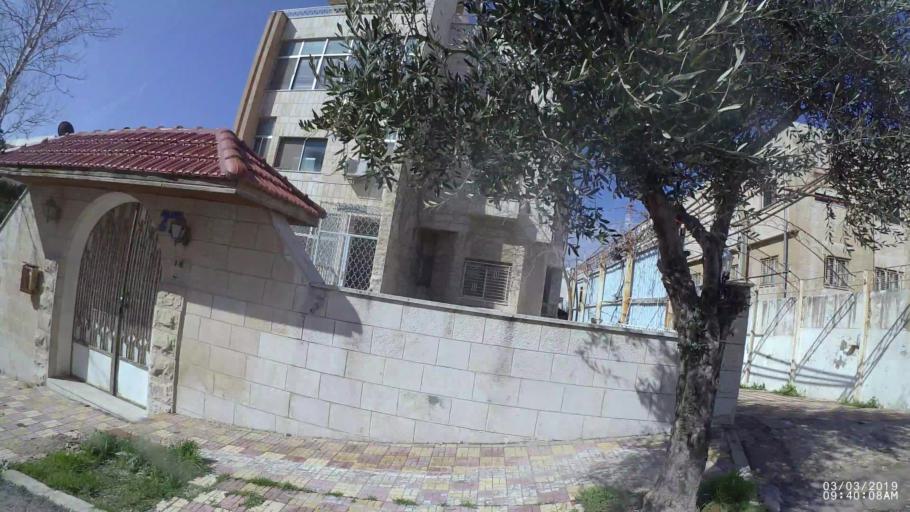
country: JO
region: Amman
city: Al Jubayhah
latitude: 31.9989
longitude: 35.8985
